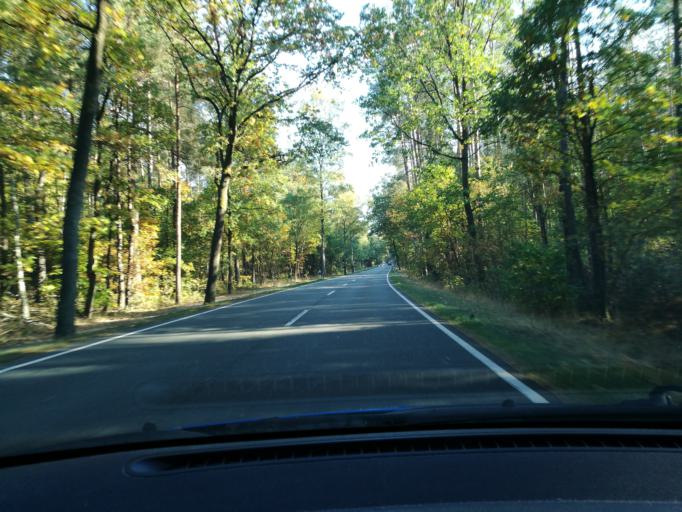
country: DE
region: Lower Saxony
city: Karwitz
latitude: 53.1247
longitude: 10.9799
